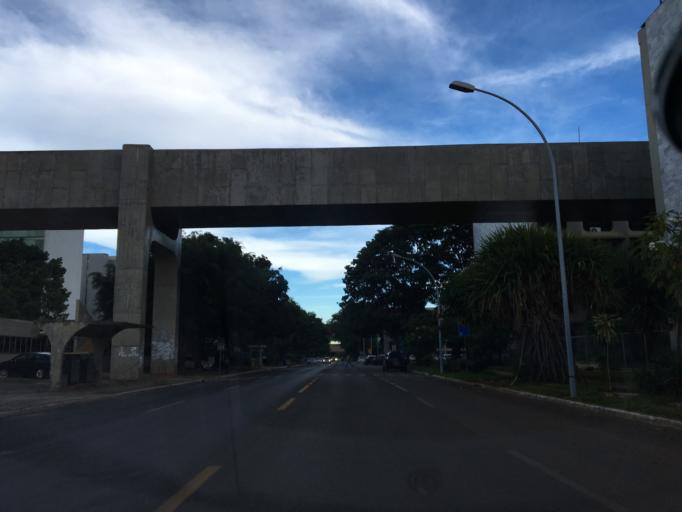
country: BR
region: Federal District
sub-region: Brasilia
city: Brasilia
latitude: -15.8003
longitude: -47.8717
